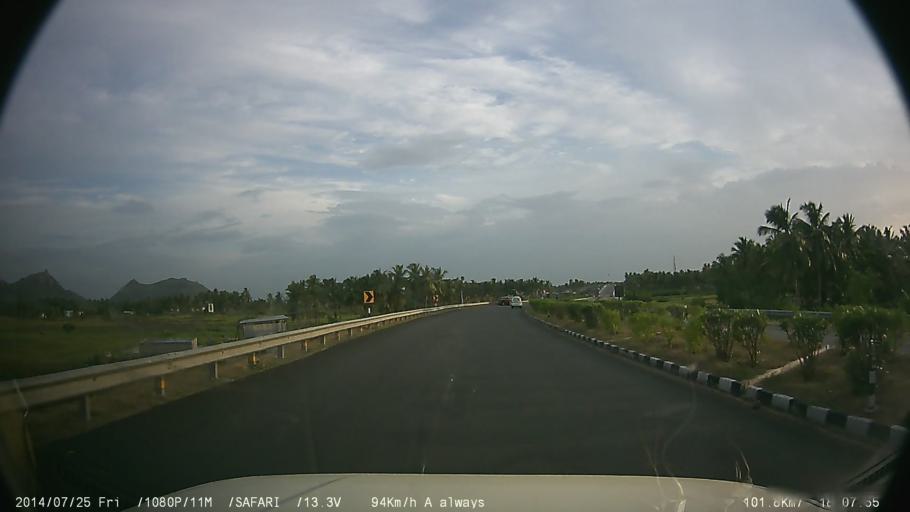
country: IN
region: Tamil Nadu
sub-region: Krishnagiri
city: Kaverippattanam
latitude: 12.4069
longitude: 78.2234
